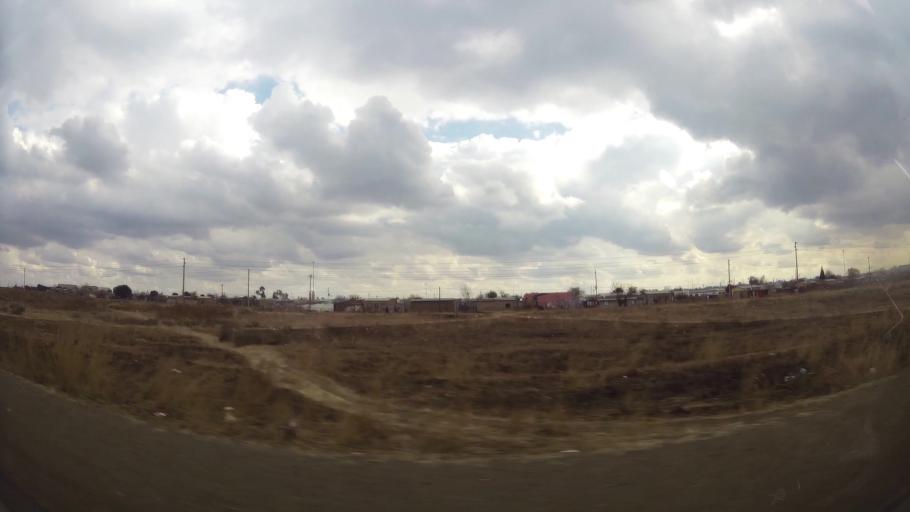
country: ZA
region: Orange Free State
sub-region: Fezile Dabi District Municipality
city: Sasolburg
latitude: -26.8597
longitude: 27.8882
